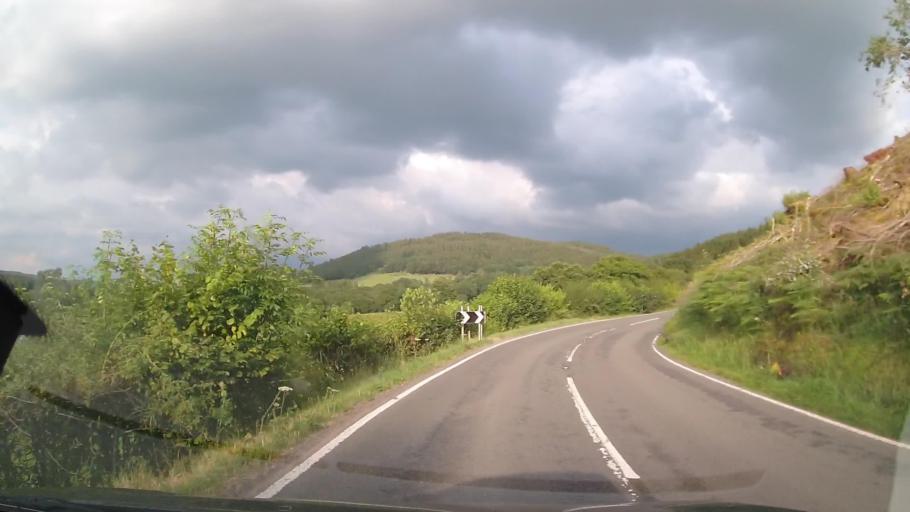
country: GB
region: Wales
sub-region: Gwynedd
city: Bala
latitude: 52.9066
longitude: -3.5324
